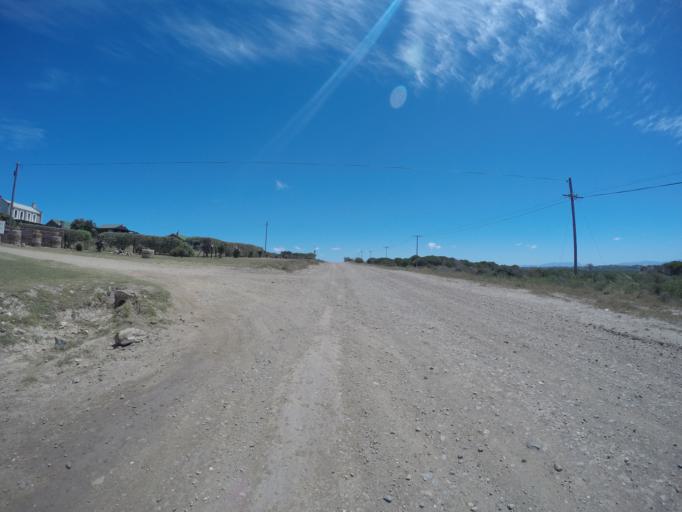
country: ZA
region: Western Cape
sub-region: Eden District Municipality
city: Riversdale
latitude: -34.4181
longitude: 20.8502
